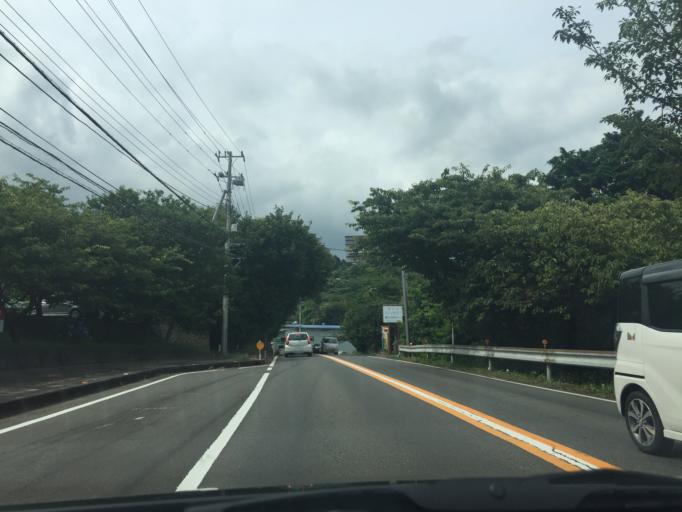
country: JP
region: Shizuoka
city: Shimoda
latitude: 34.7639
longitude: 139.0227
